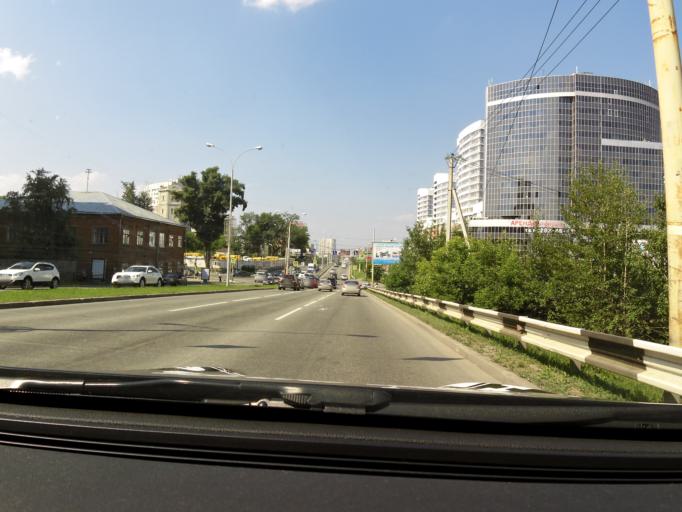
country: RU
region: Sverdlovsk
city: Yekaterinburg
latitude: 56.8283
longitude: 60.5850
